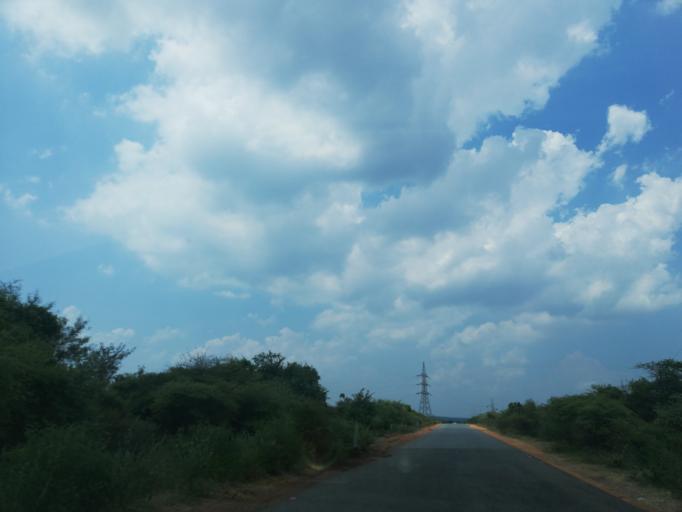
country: IN
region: Andhra Pradesh
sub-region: Guntur
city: Macherla
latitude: 16.5653
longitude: 79.3482
